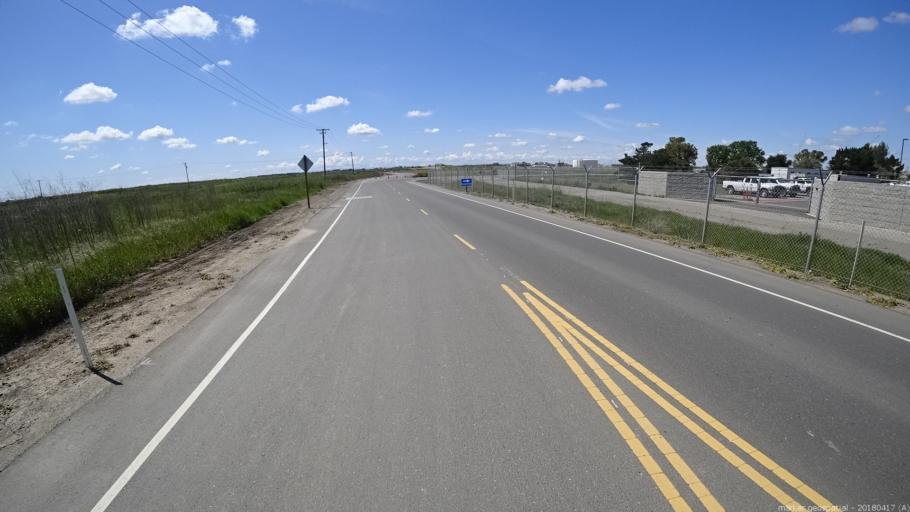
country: US
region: California
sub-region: Sacramento County
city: Laguna
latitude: 38.4443
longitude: -121.4639
